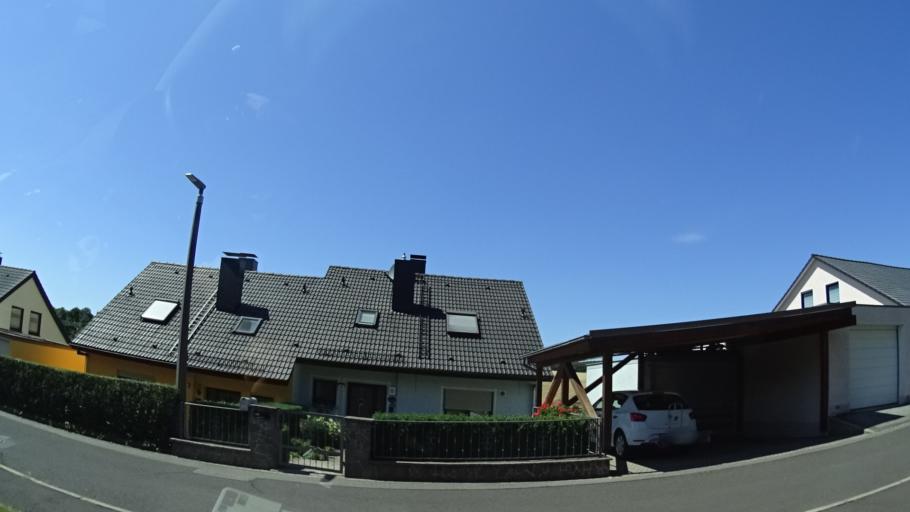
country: DE
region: Bavaria
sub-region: Regierungsbezirk Unterfranken
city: Guntersleben
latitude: 49.8720
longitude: 9.9105
